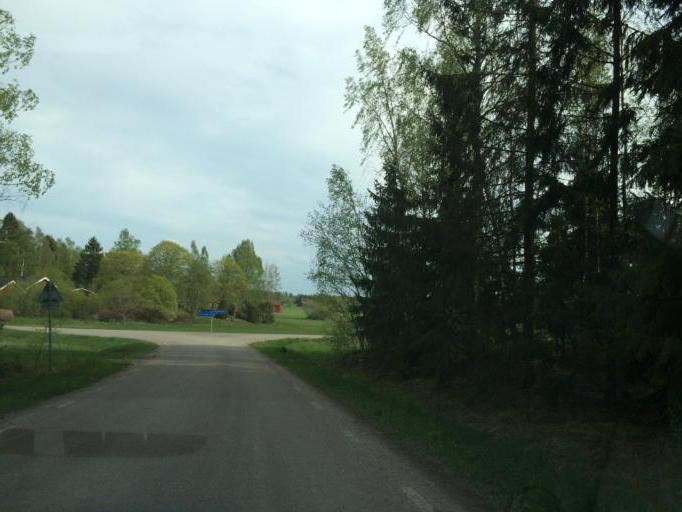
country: SE
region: Vaestmanland
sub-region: Hallstahammars Kommun
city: Hallstahammar
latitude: 59.6010
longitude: 16.1005
